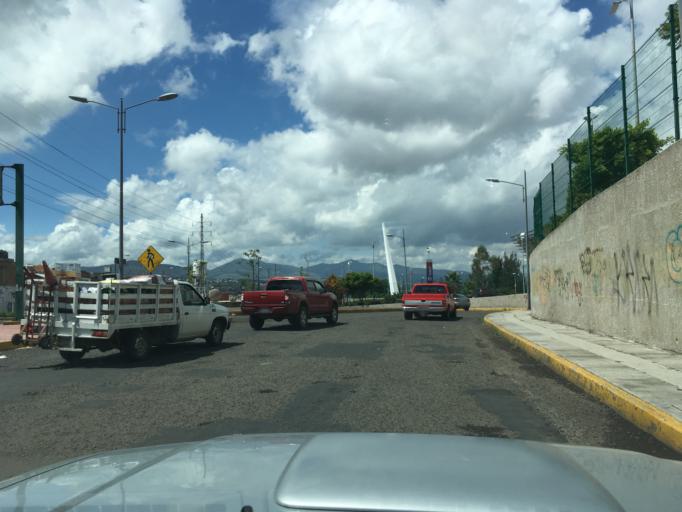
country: MX
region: Michoacan
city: Morelia
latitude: 19.7233
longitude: -101.1967
